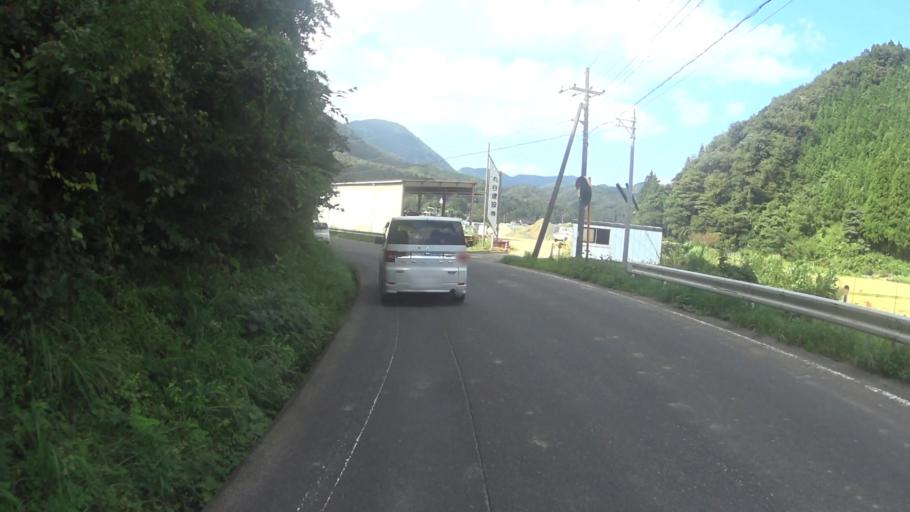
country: JP
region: Kyoto
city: Miyazu
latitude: 35.7180
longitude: 135.2575
